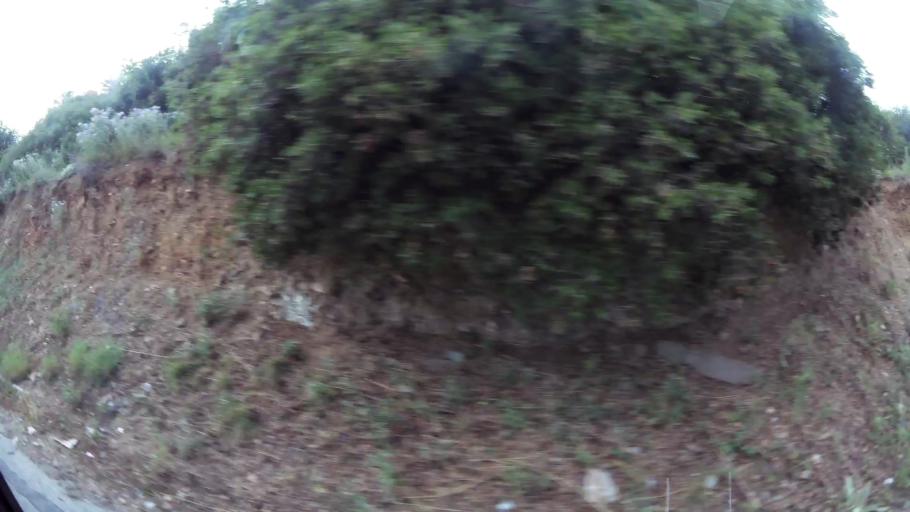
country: GR
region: Central Macedonia
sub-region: Nomos Thessalonikis
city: Pefka
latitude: 40.6627
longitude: 22.9867
